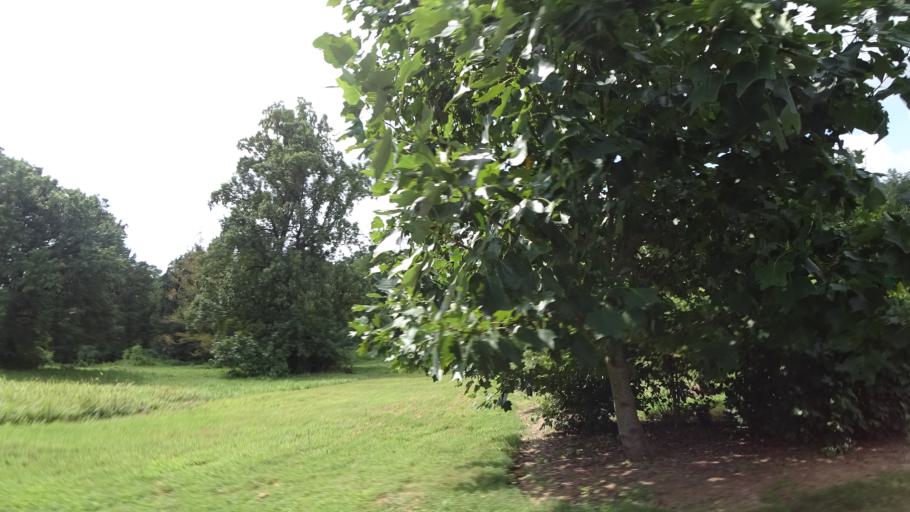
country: US
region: Maryland
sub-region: Prince George's County
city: Colmar Manor
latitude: 38.9120
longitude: -76.9636
